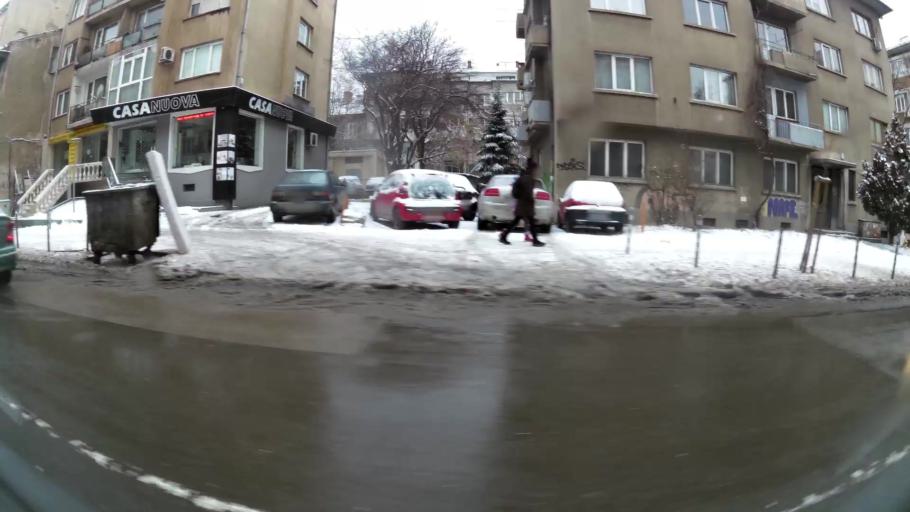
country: BG
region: Sofia-Capital
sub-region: Stolichna Obshtina
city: Sofia
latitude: 42.6953
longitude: 23.3515
